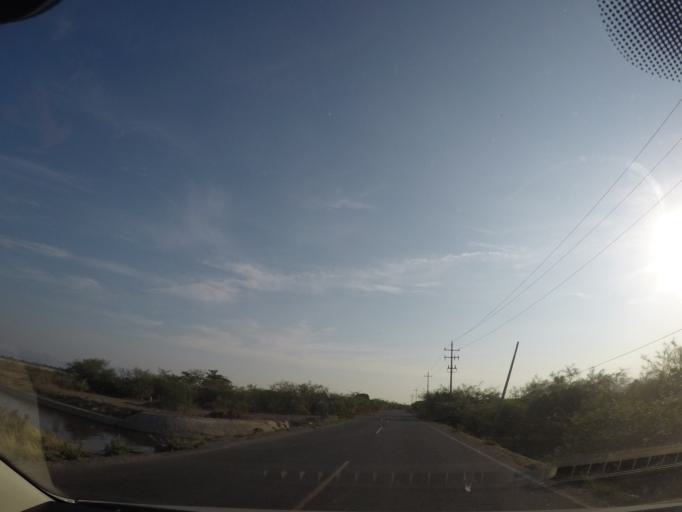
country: MX
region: Oaxaca
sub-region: Santo Domingo Tehuantepec
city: La Noria
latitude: 16.2280
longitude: -95.1858
